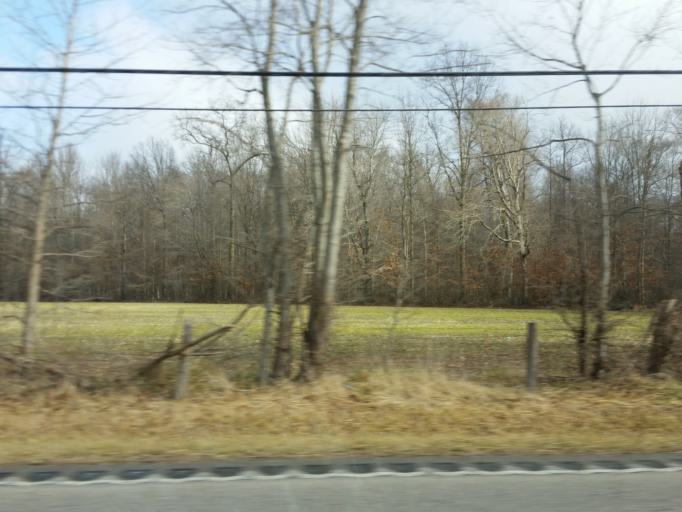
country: US
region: Indiana
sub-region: Jefferson County
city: North Madison
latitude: 38.8149
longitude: -85.4604
